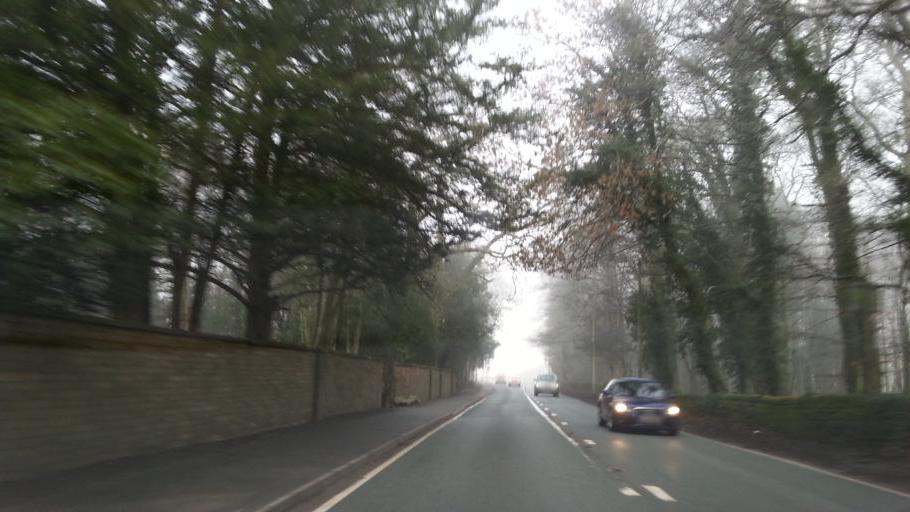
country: GB
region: England
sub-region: Cheshire East
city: Alderley Edge
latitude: 53.2716
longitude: -2.2390
